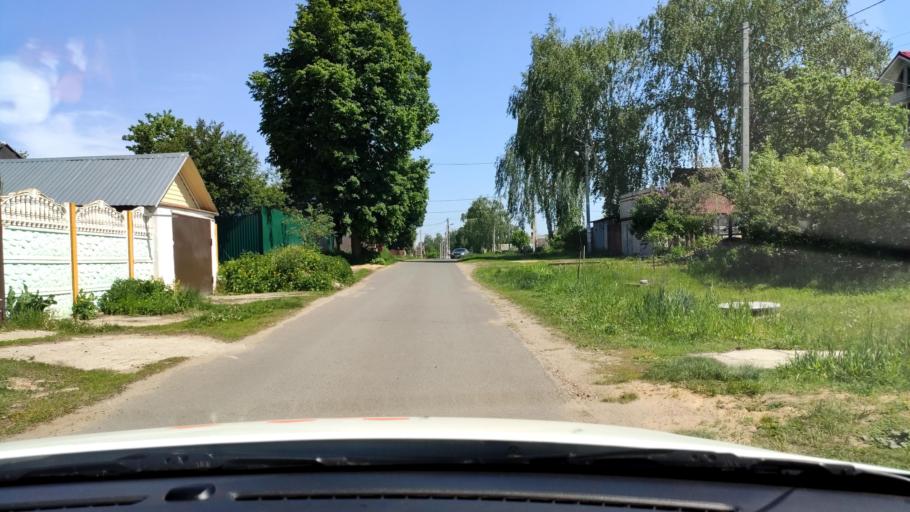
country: RU
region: Tatarstan
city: Osinovo
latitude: 55.8297
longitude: 48.8718
